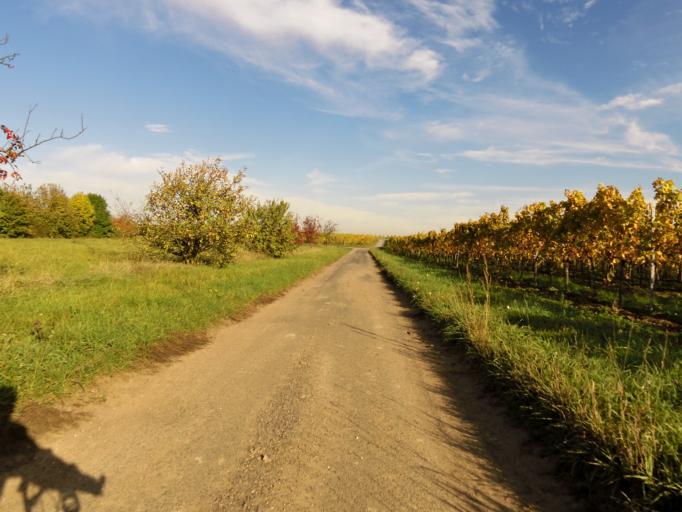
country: DE
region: Rheinland-Pfalz
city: Friedelsheim
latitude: 49.4479
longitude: 8.2063
